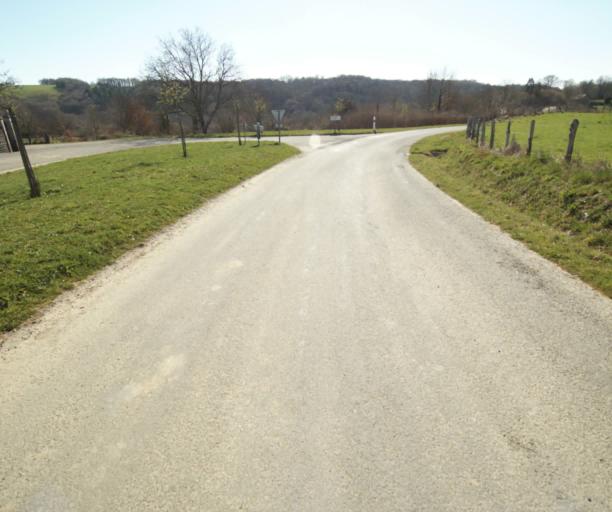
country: FR
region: Limousin
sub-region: Departement de la Correze
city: Chamboulive
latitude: 45.4239
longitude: 1.6464
